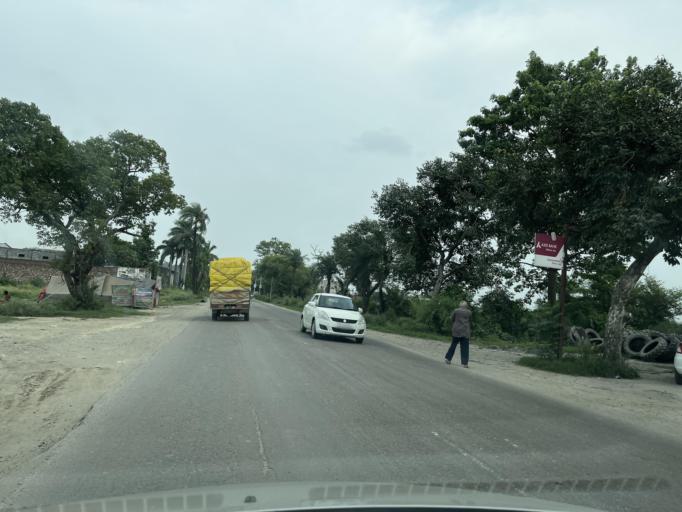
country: IN
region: Uttar Pradesh
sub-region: Rampur
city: Bilaspur
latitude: 29.0358
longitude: 79.2563
